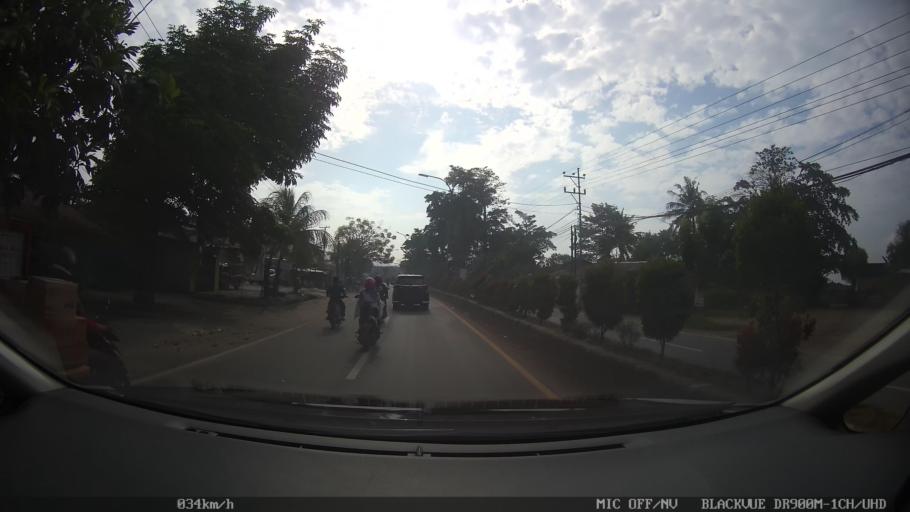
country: ID
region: Lampung
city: Bandarlampung
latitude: -5.4439
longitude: 105.2828
